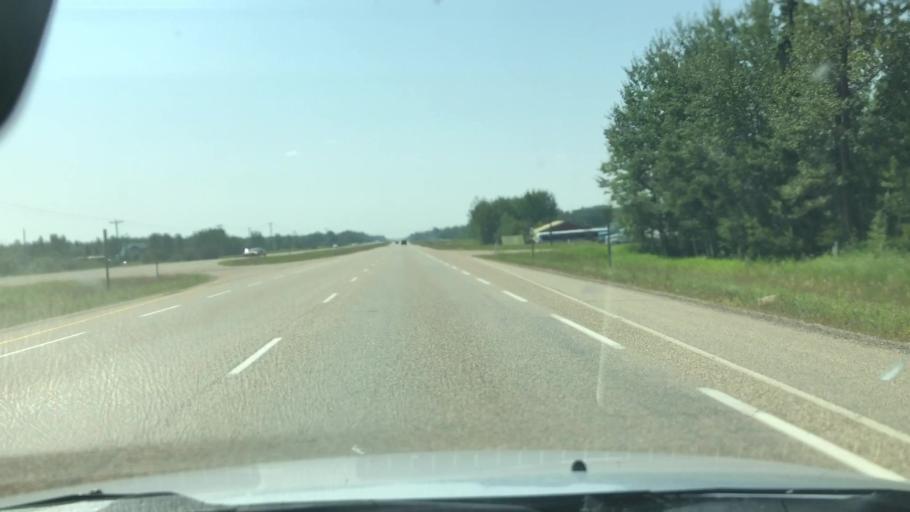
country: CA
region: Alberta
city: Devon
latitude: 53.4331
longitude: -113.7632
